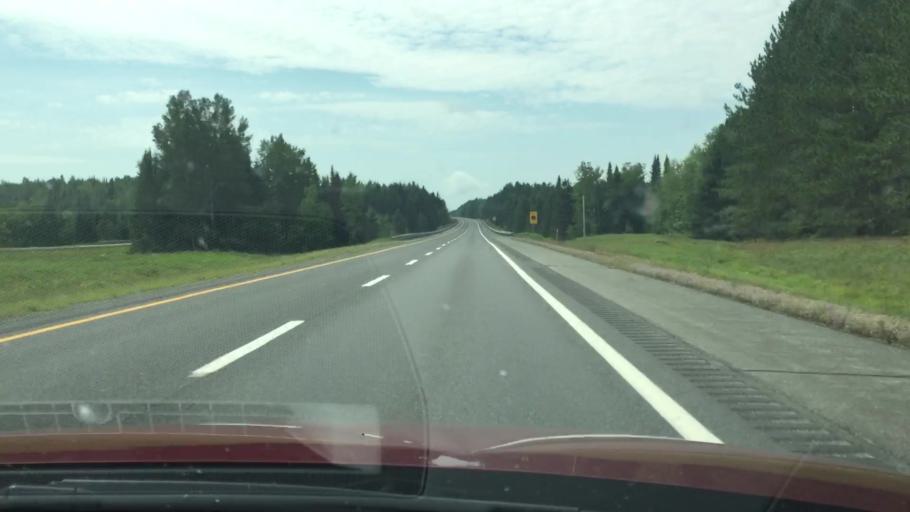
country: US
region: Maine
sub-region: Aroostook County
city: Hodgdon
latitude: 46.1391
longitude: -68.0753
